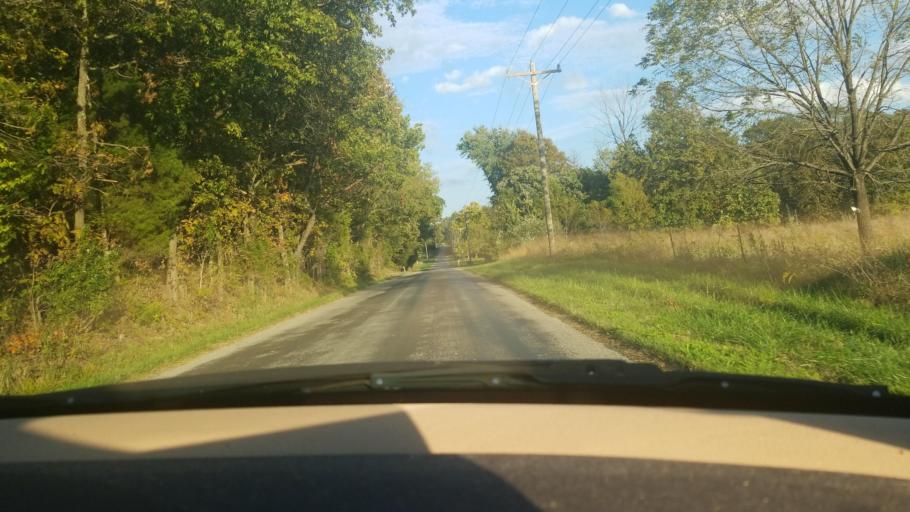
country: US
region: Illinois
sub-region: Saline County
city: Carrier Mills
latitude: 37.7710
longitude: -88.7634
